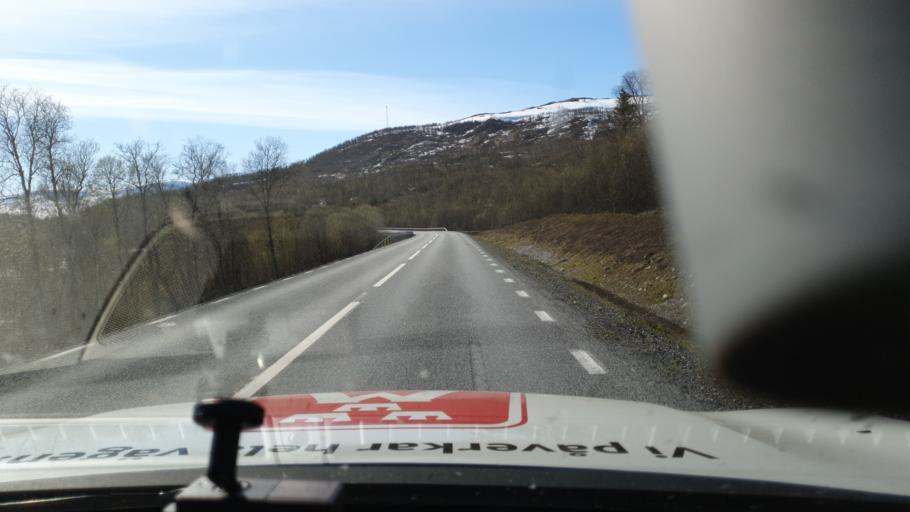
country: NO
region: Nordland
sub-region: Rana
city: Mo i Rana
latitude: 66.0520
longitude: 14.9304
